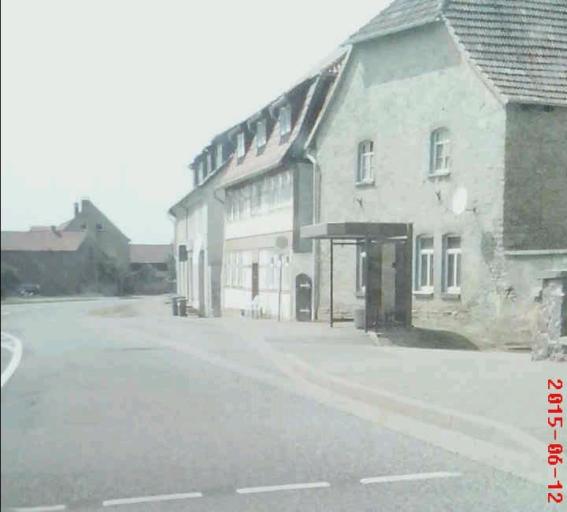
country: DE
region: Saxony-Anhalt
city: Bennungen
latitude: 51.4616
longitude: 11.1187
